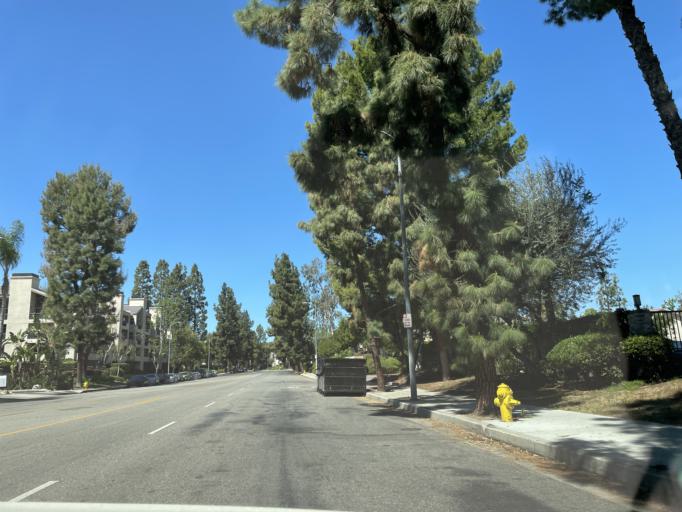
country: US
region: California
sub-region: Los Angeles County
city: Woodland Hills
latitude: 34.1733
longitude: -118.5985
